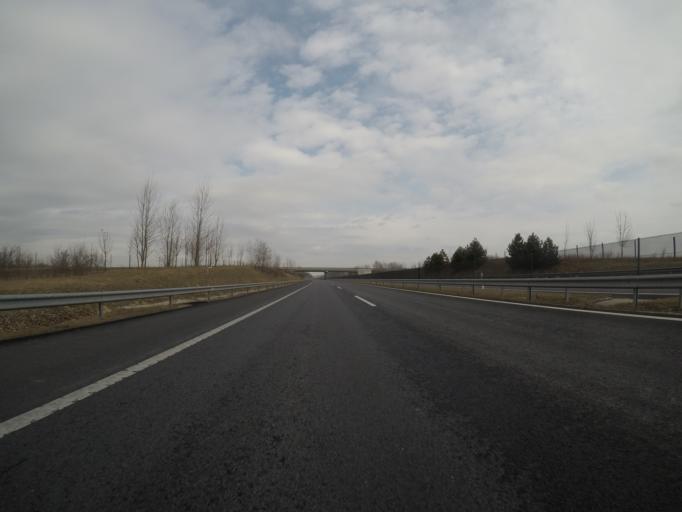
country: HU
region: Zala
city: Zalakomar
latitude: 46.4931
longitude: 17.1238
